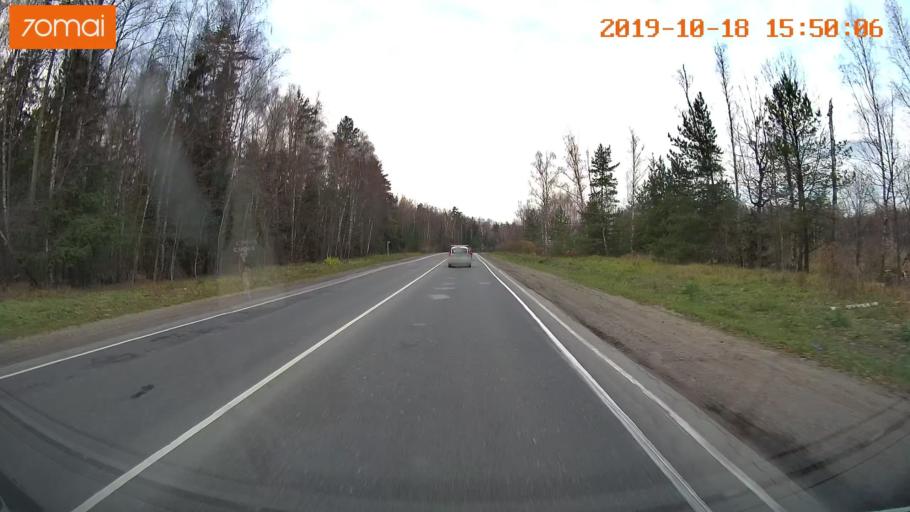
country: RU
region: Vladimir
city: Kommunar
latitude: 56.0294
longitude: 40.5648
